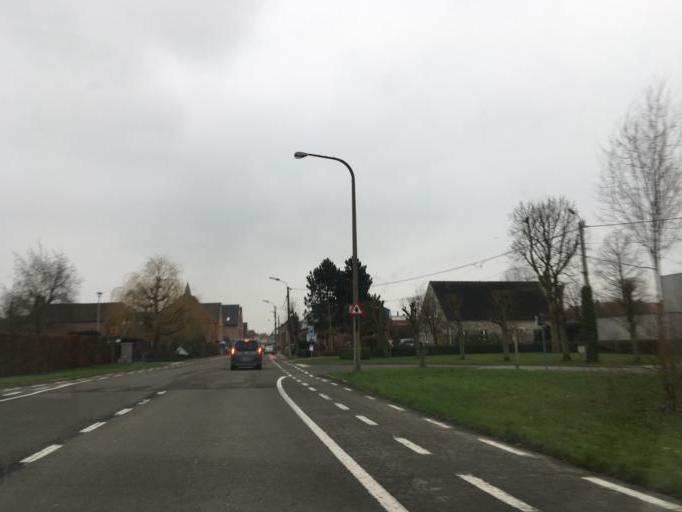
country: BE
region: Flanders
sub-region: Provincie West-Vlaanderen
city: Izegem
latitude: 50.8791
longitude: 3.1776
